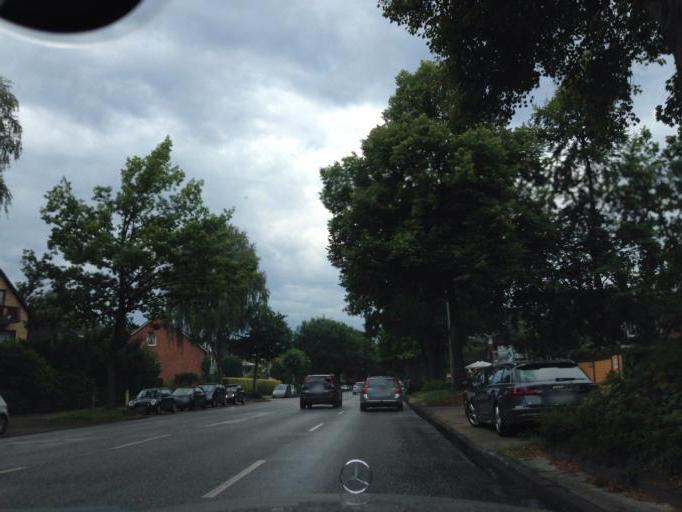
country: DE
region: Hamburg
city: Sasel
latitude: 53.6451
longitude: 10.1006
